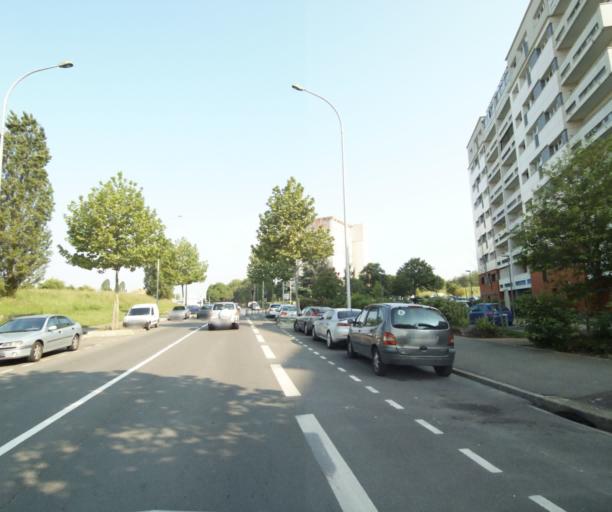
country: FR
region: Ile-de-France
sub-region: Departement du Val-d'Oise
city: Cormeilles-en-Parisis
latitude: 48.9539
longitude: 2.2169
